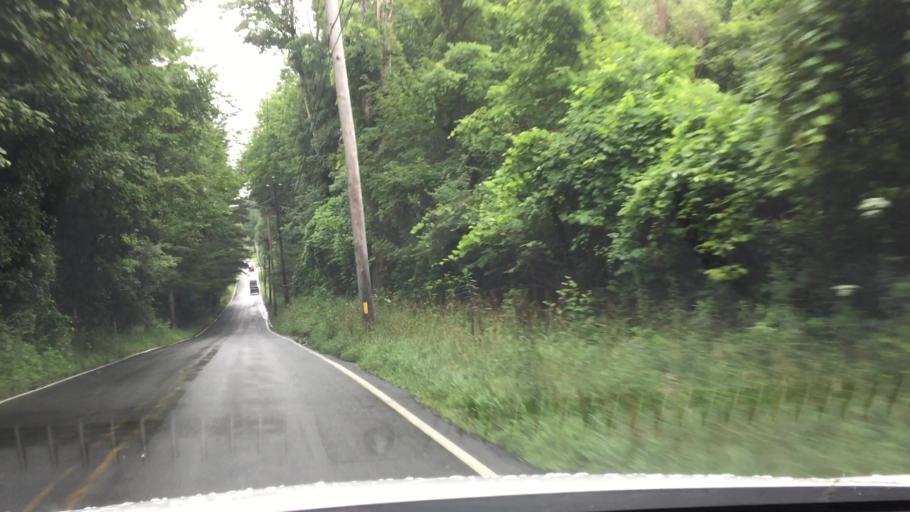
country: US
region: Massachusetts
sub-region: Berkshire County
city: Pittsfield
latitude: 42.4206
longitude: -73.2907
